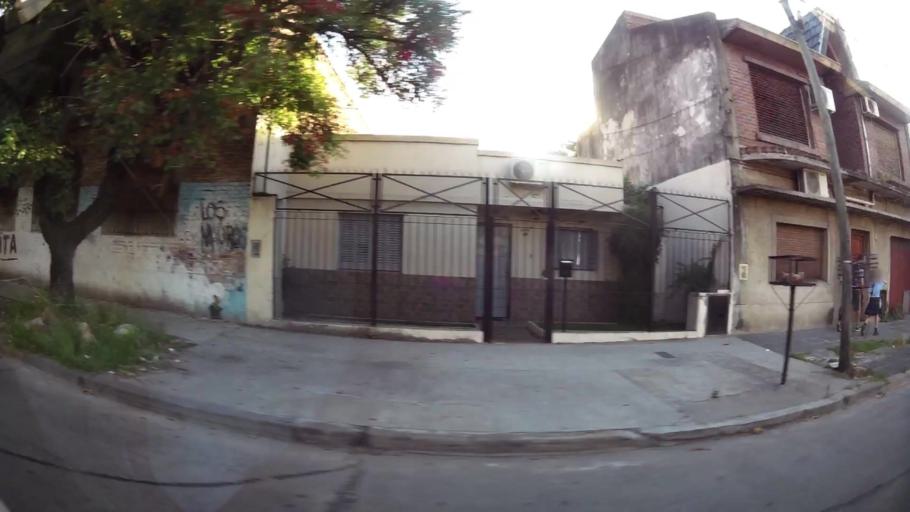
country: AR
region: Buenos Aires
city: Caseros
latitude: -34.5615
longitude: -58.5658
